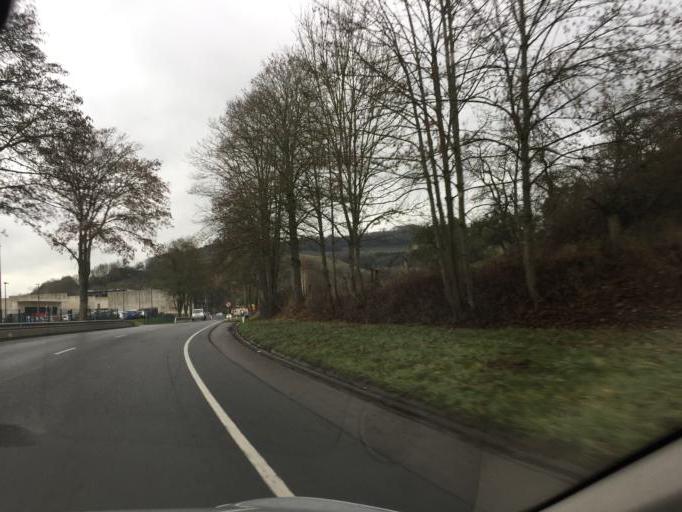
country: LU
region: Diekirch
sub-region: Canton de Diekirch
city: Bettendorf
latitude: 49.8721
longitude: 6.1943
